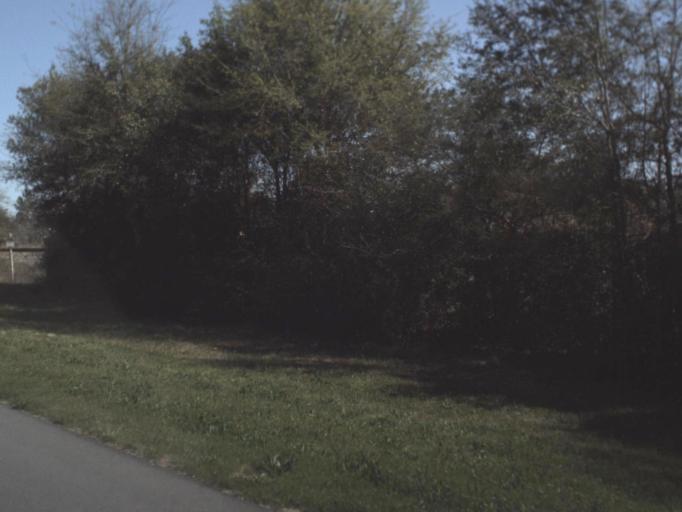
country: US
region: Florida
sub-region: Walton County
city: DeFuniak Springs
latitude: 30.7383
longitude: -86.1723
